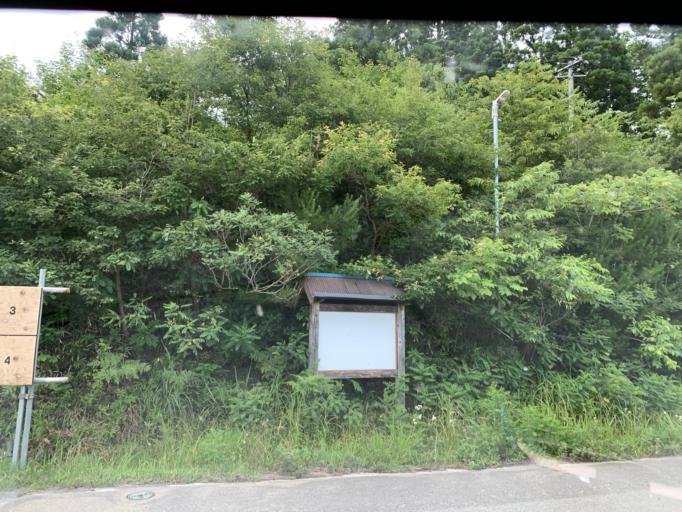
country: JP
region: Iwate
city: Ichinoseki
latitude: 38.9051
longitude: 141.0118
